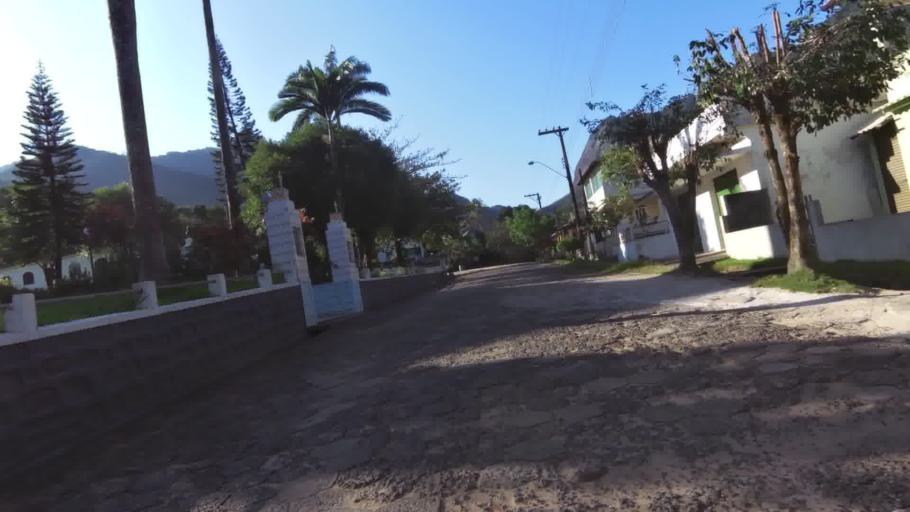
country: BR
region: Espirito Santo
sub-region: Alfredo Chaves
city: Alfredo Chaves
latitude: -20.5800
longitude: -40.6976
